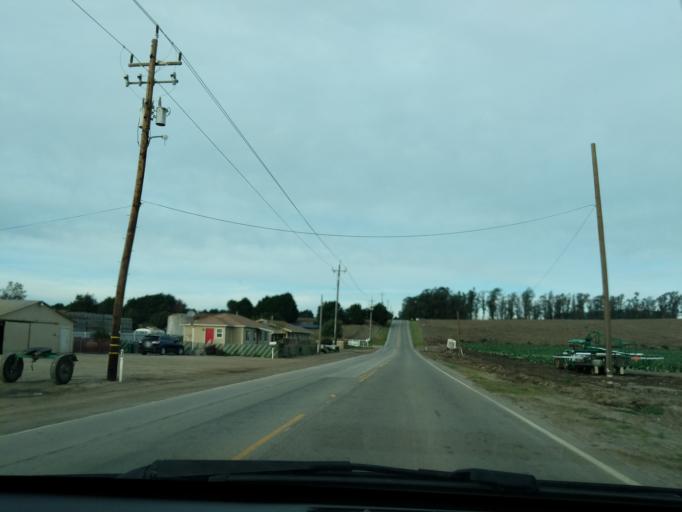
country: US
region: California
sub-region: Santa Barbara County
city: Guadalupe
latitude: 35.0167
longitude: -120.5651
